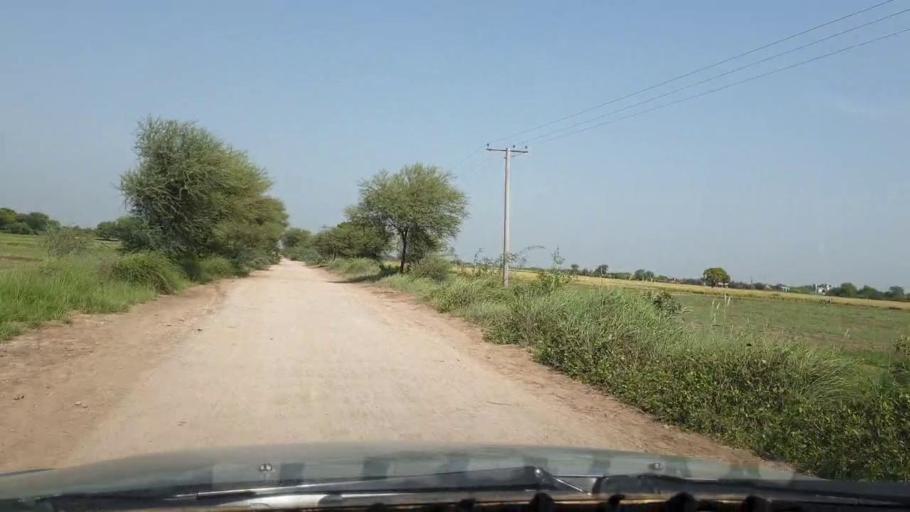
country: PK
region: Sindh
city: Tando Muhammad Khan
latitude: 25.1525
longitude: 68.6337
